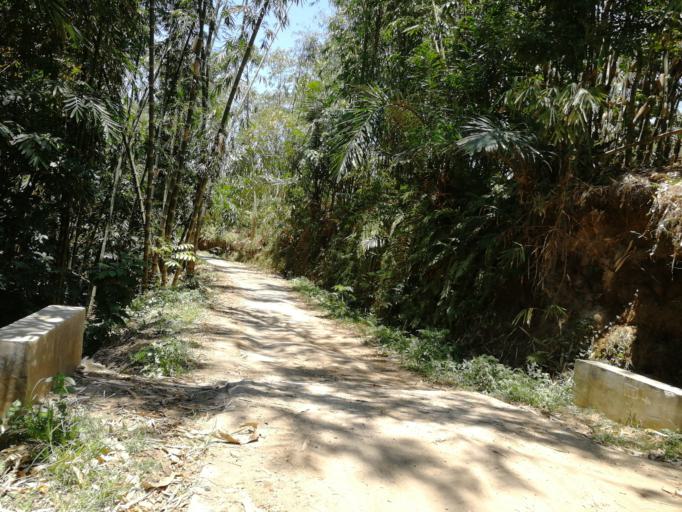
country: ID
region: West Nusa Tenggara
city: Tetebatu
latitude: -8.5454
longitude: 116.4203
